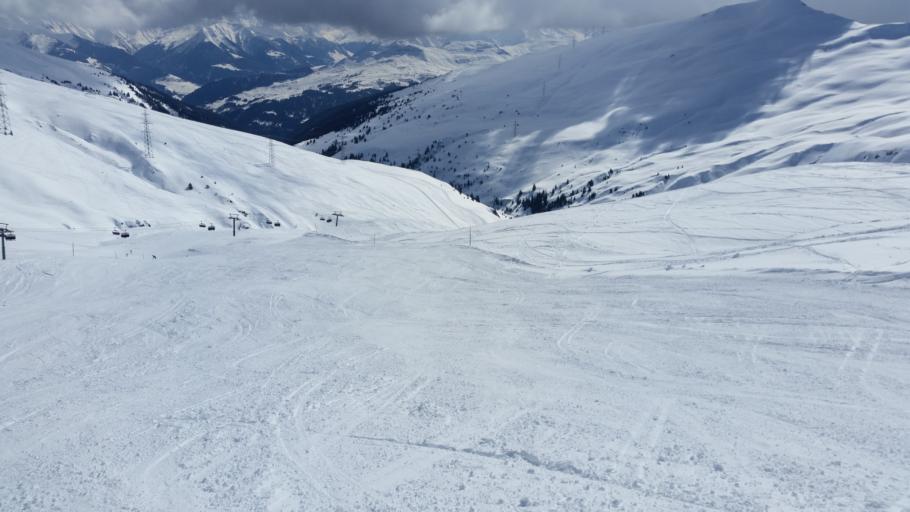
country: CH
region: Grisons
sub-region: Surselva District
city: Ilanz
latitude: 46.8520
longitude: 9.1589
